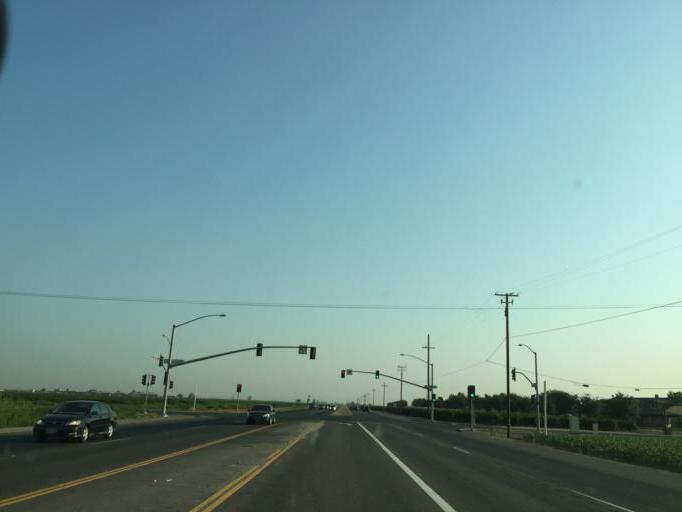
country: US
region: California
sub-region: Tulare County
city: London
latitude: 36.4577
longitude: -119.3945
